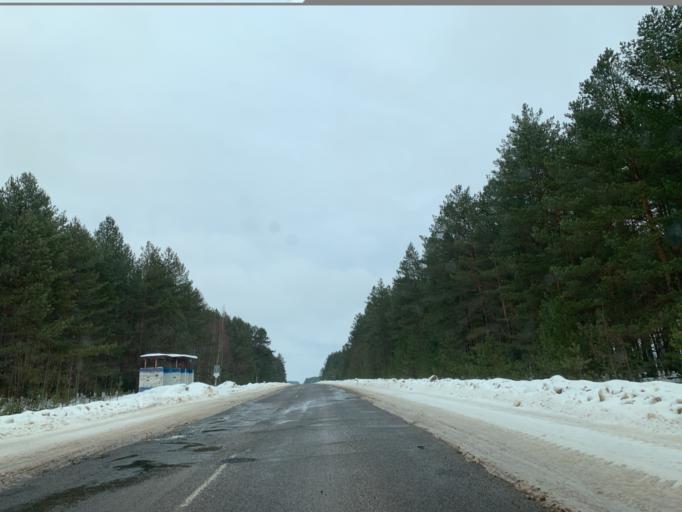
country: BY
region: Minsk
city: Il'ya
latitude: 54.3305
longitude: 27.2531
